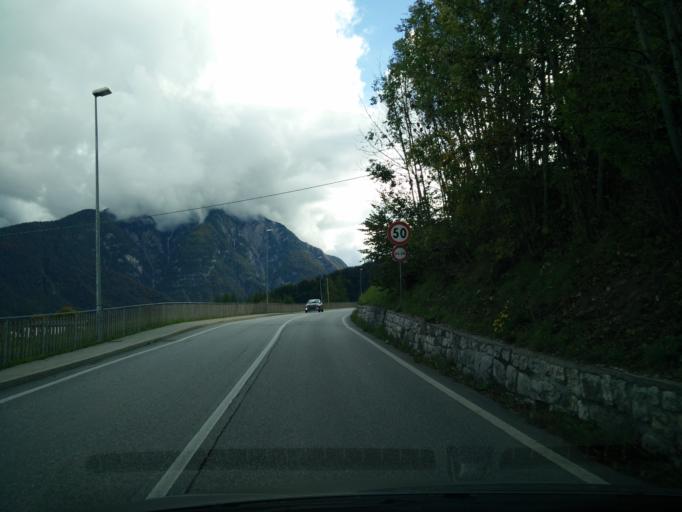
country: IT
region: Veneto
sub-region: Provincia di Belluno
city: Calalzo di Cadore
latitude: 46.4390
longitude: 12.3801
